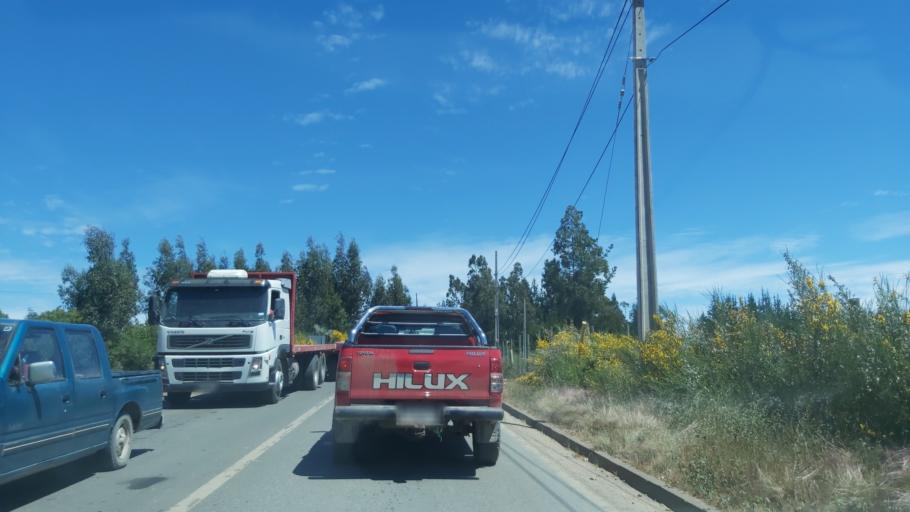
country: CL
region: Maule
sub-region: Provincia de Talca
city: Constitucion
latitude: -35.3897
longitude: -72.4240
